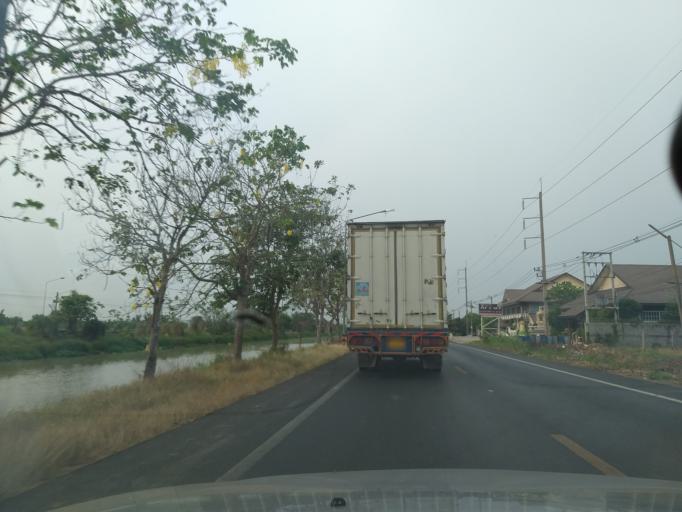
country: TH
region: Bangkok
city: Nong Chok
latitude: 13.9638
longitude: 100.8955
